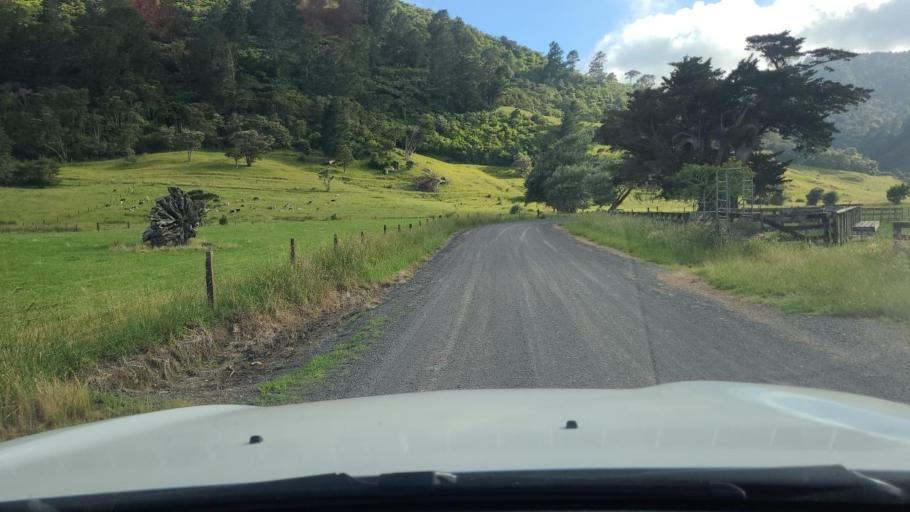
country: NZ
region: Bay of Plenty
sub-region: Western Bay of Plenty District
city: Katikati
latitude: -37.5620
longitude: 175.7490
